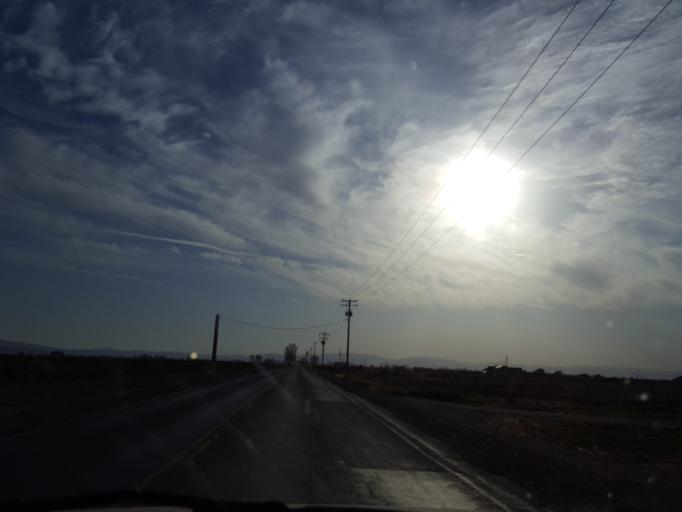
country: US
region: California
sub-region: Merced County
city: Los Banos
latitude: 37.0997
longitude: -120.8382
